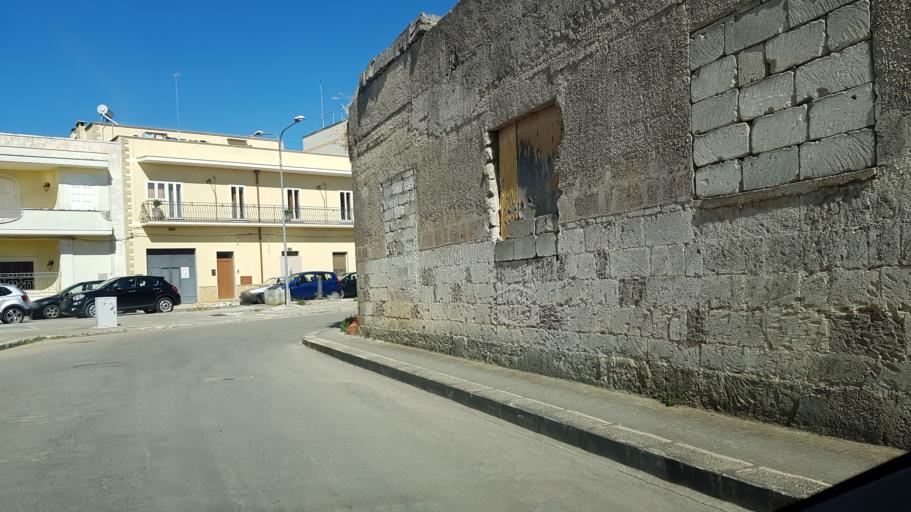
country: IT
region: Apulia
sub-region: Provincia di Brindisi
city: San Vito dei Normanni
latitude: 40.6602
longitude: 17.6998
